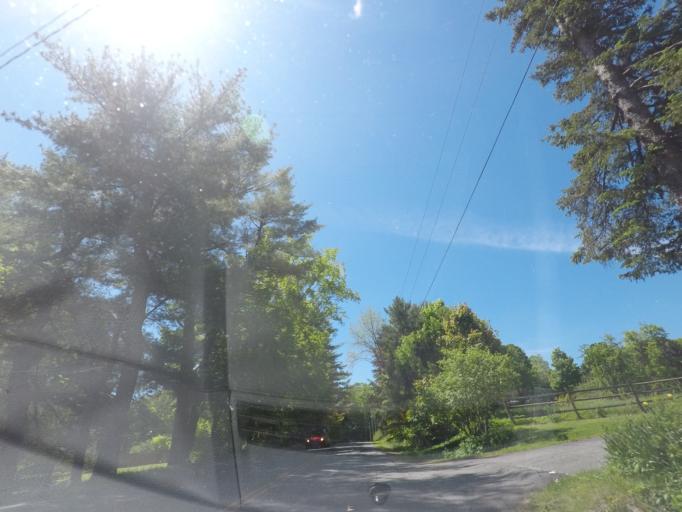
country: US
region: Maine
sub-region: Kennebec County
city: Hallowell
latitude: 44.2794
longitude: -69.7961
